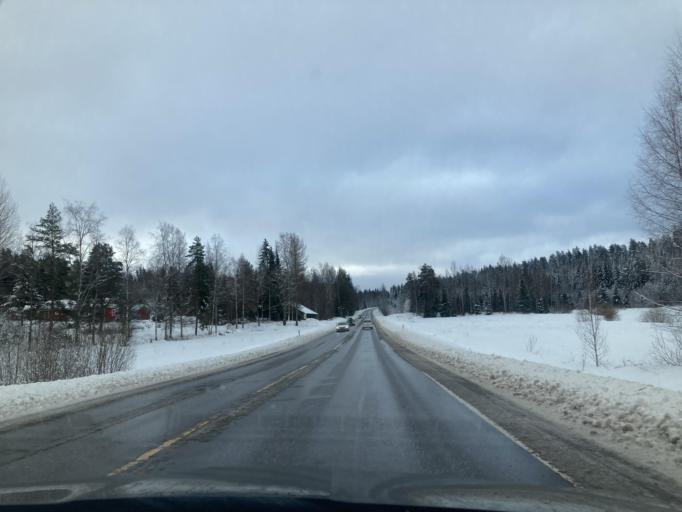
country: FI
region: Paijanne Tavastia
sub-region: Lahti
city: Padasjoki
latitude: 61.3386
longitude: 25.2601
